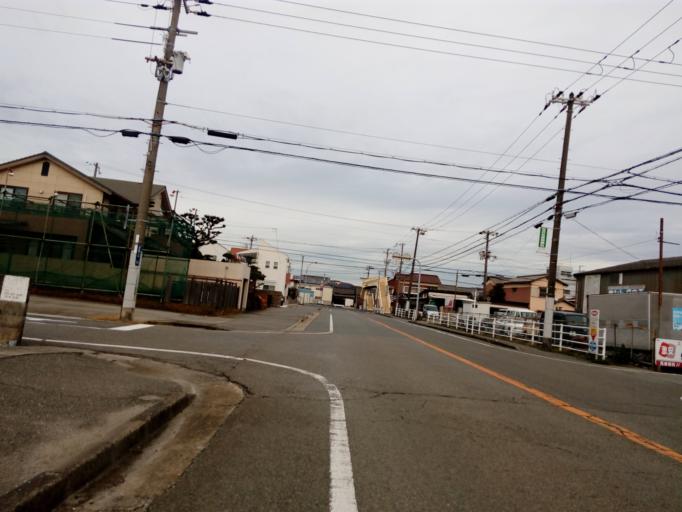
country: JP
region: Hyogo
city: Tatsunocho-tominaga
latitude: 34.7933
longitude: 134.6073
